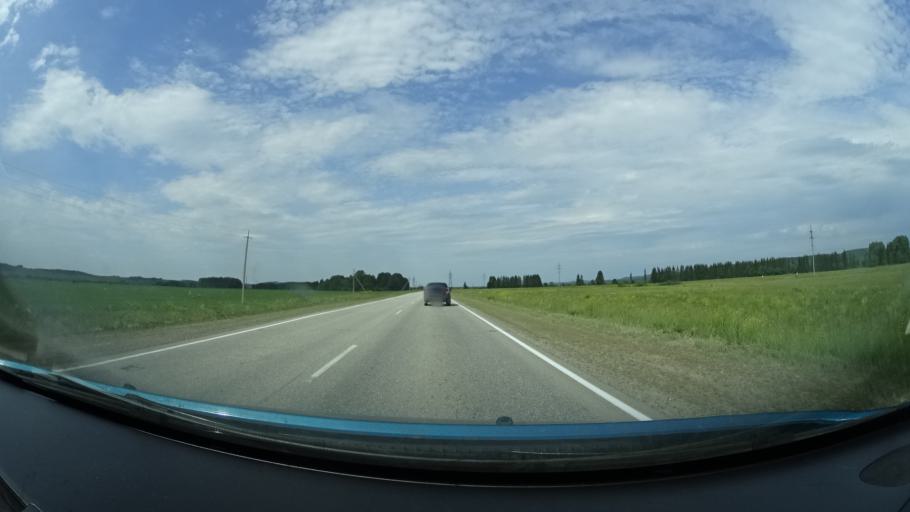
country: RU
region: Perm
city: Barda
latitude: 57.0638
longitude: 55.5422
